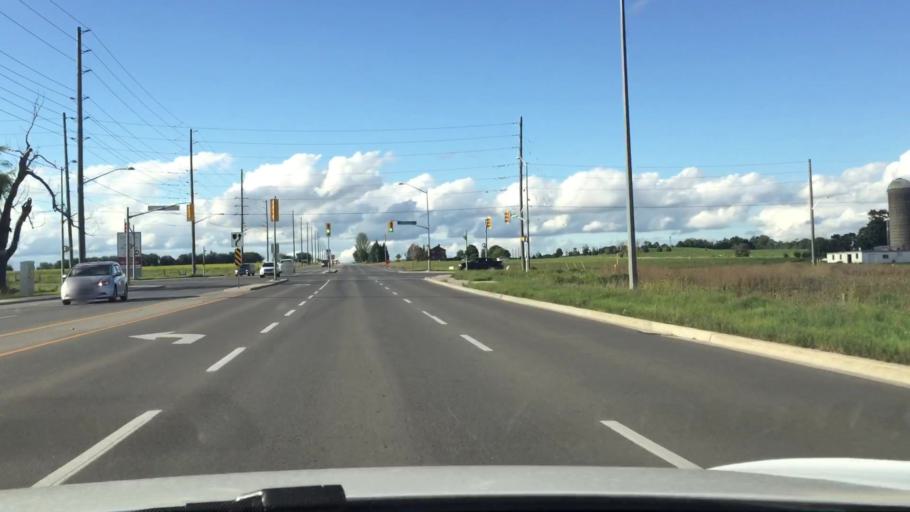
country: CA
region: Ontario
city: Oshawa
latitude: 43.9561
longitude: -78.8568
